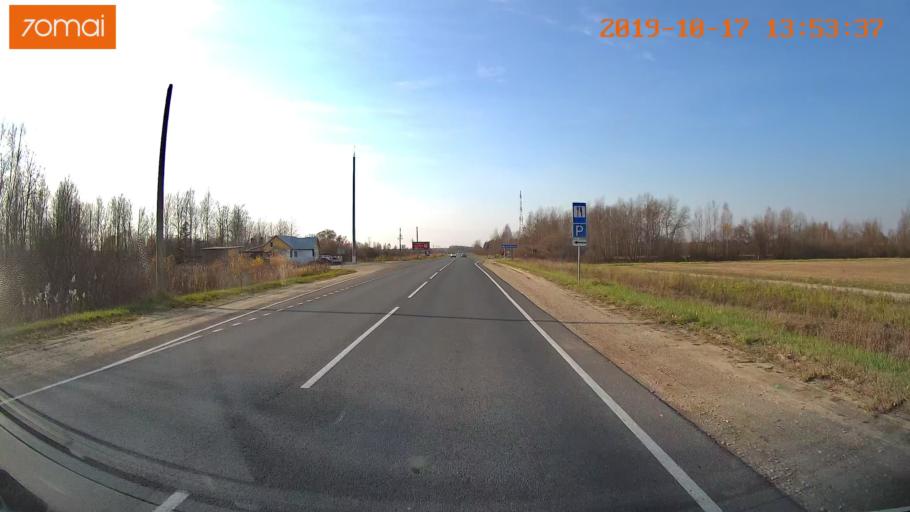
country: RU
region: Rjazan
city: Spas-Klepiki
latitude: 55.1429
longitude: 40.3364
